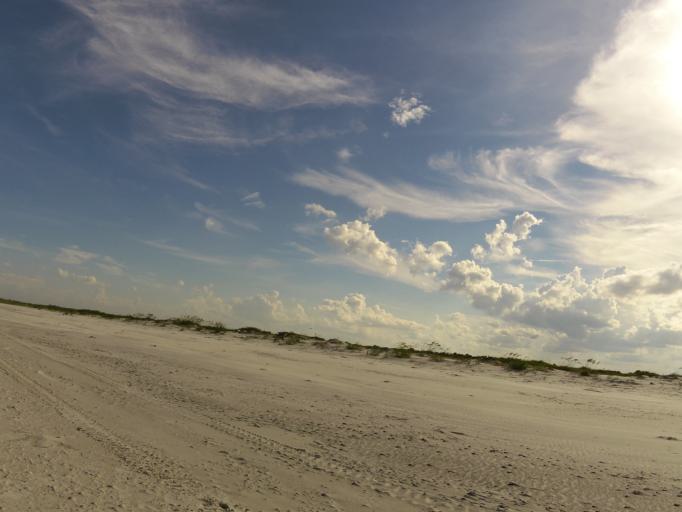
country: US
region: Florida
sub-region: Duval County
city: Atlantic Beach
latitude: 30.4453
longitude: -81.4092
